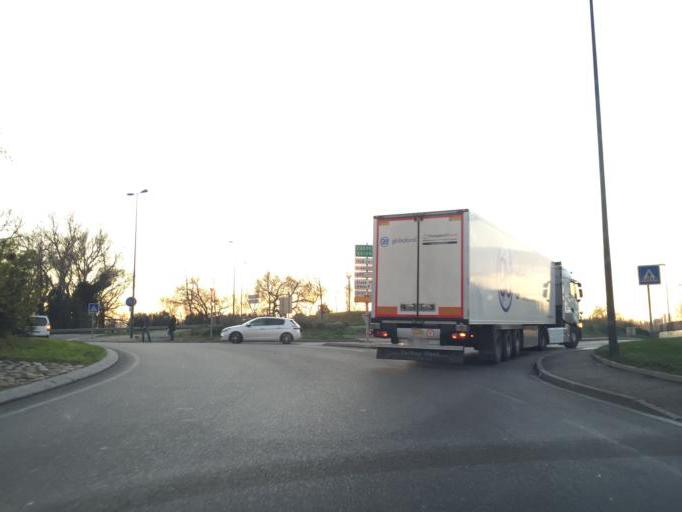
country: FR
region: Provence-Alpes-Cote d'Azur
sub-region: Departement du Vaucluse
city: Cavaillon
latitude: 43.8282
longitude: 5.0340
